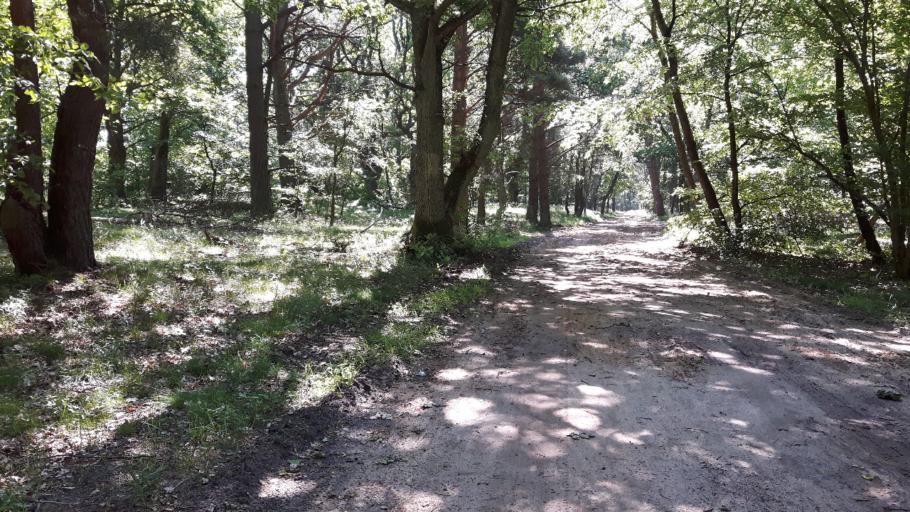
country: PL
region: Pomeranian Voivodeship
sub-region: Powiat slupski
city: Smoldzino
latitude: 54.6775
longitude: 17.1540
